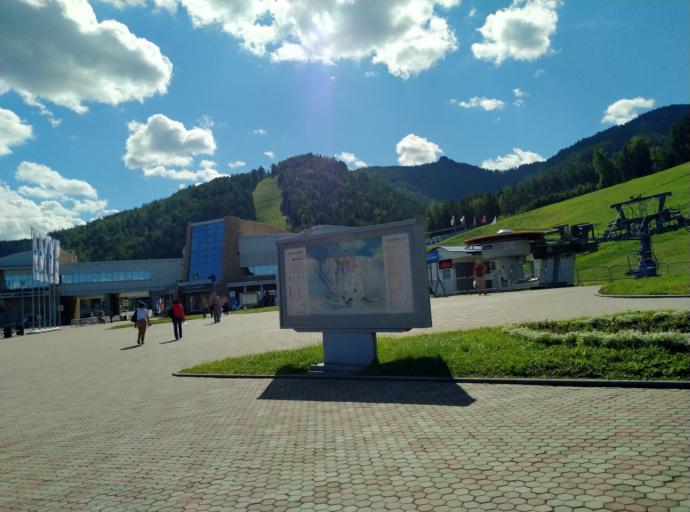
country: RU
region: Krasnoyarskiy
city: Krasnoyarsk
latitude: 55.9623
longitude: 92.7941
